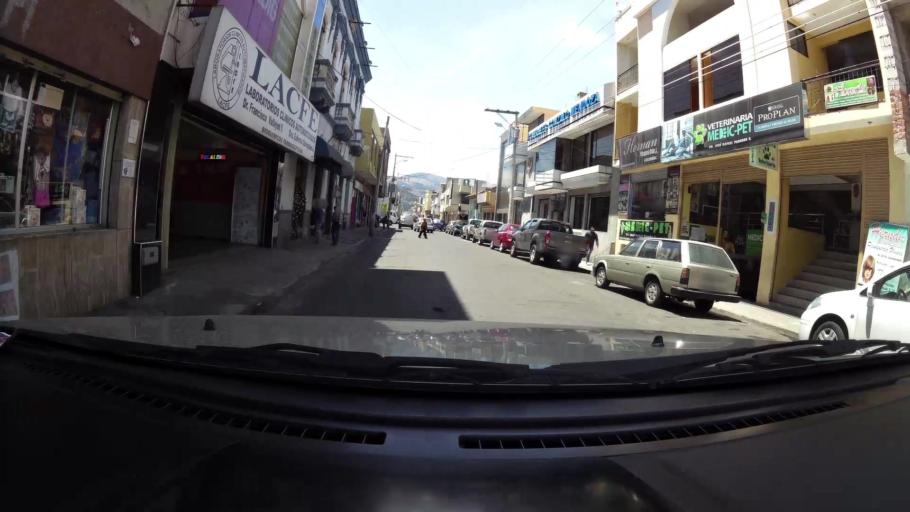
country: EC
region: Chimborazo
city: Riobamba
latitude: -1.6731
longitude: -78.6520
